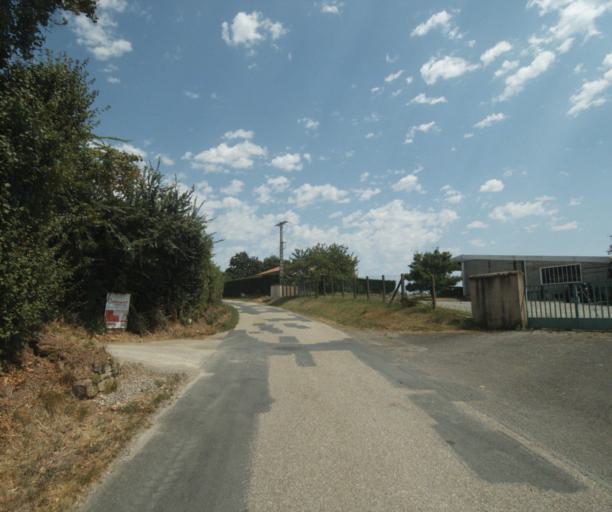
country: FR
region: Rhone-Alpes
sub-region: Departement du Rhone
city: Saint-Germain-Nuelles
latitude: 45.8426
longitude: 4.6222
